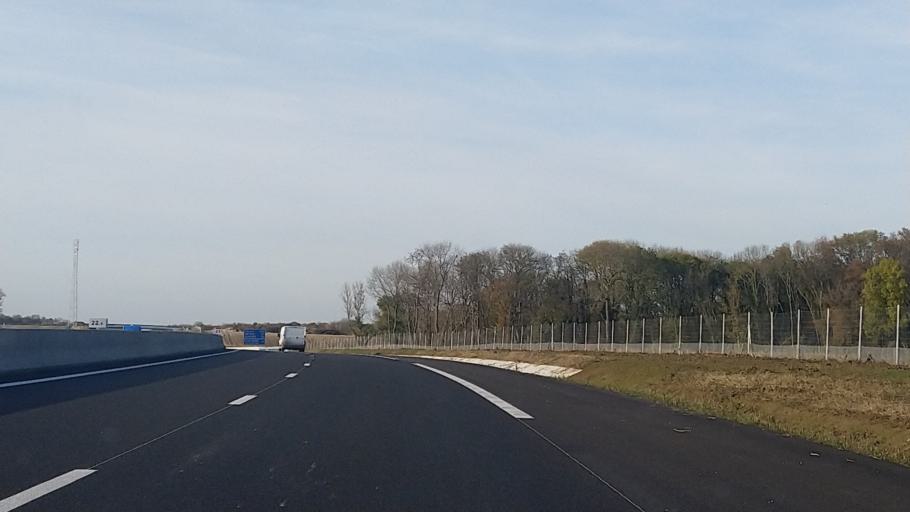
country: FR
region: Ile-de-France
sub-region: Departement du Val-d'Oise
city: Montsoult
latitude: 49.0808
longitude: 2.3290
